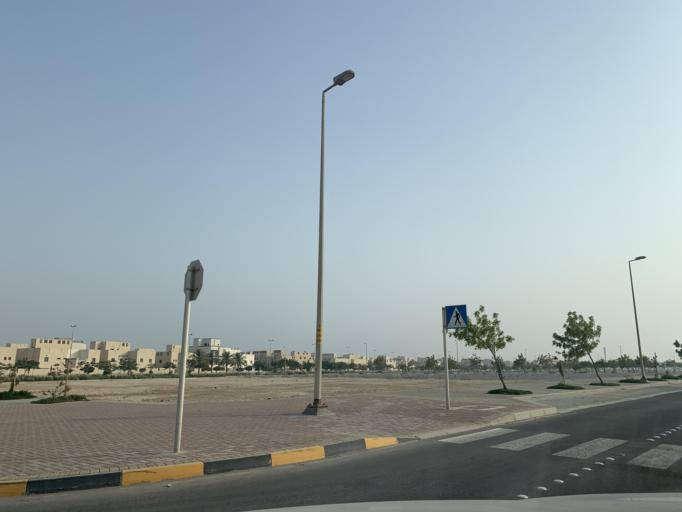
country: BH
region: Manama
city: Jidd Hafs
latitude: 26.2259
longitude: 50.4460
